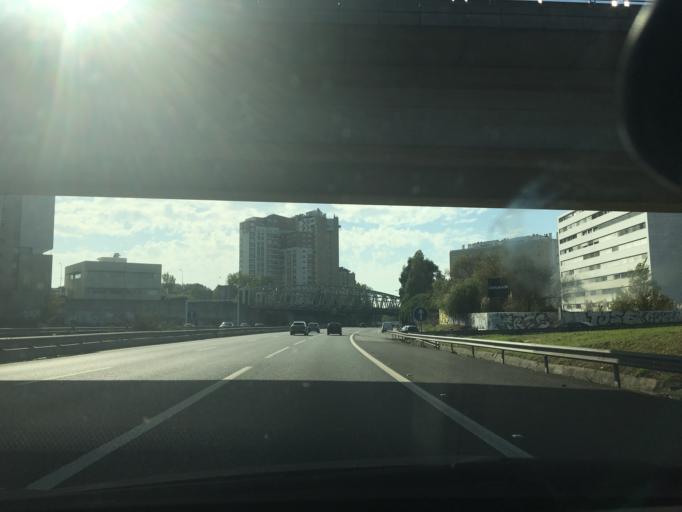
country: PT
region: Porto
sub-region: Matosinhos
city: Senhora da Hora
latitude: 41.1668
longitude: -8.6430
